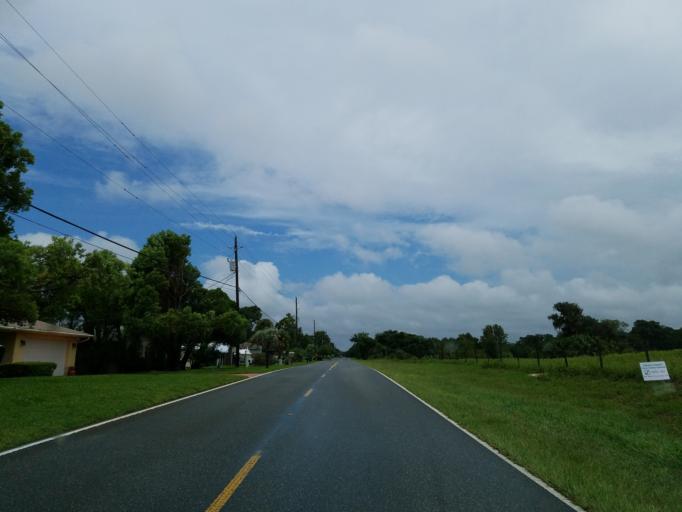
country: US
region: Florida
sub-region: Citrus County
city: Inverness
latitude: 28.8105
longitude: -82.2936
